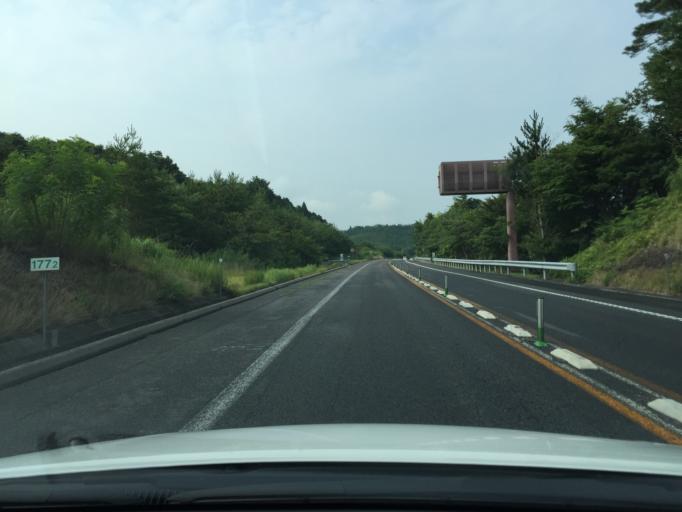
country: JP
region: Fukushima
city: Iwaki
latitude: 37.0853
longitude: 140.8420
